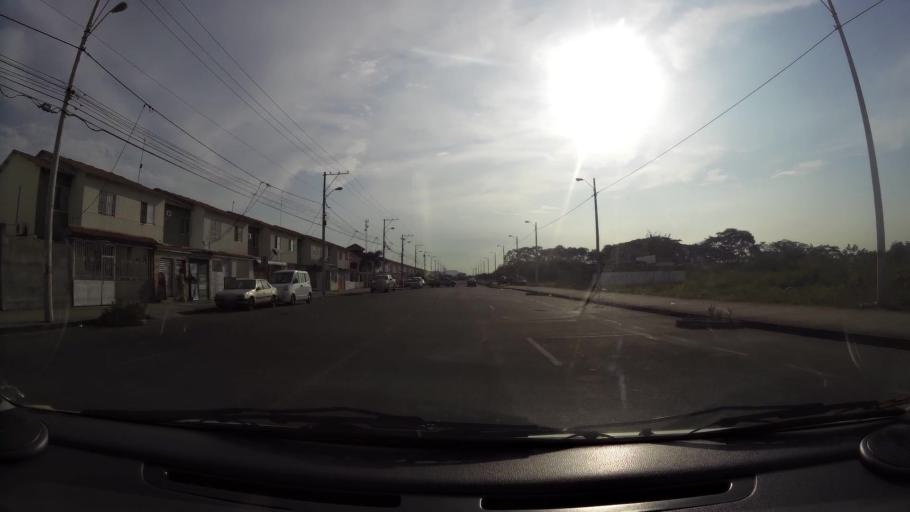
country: EC
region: Guayas
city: Eloy Alfaro
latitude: -2.0610
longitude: -79.8867
